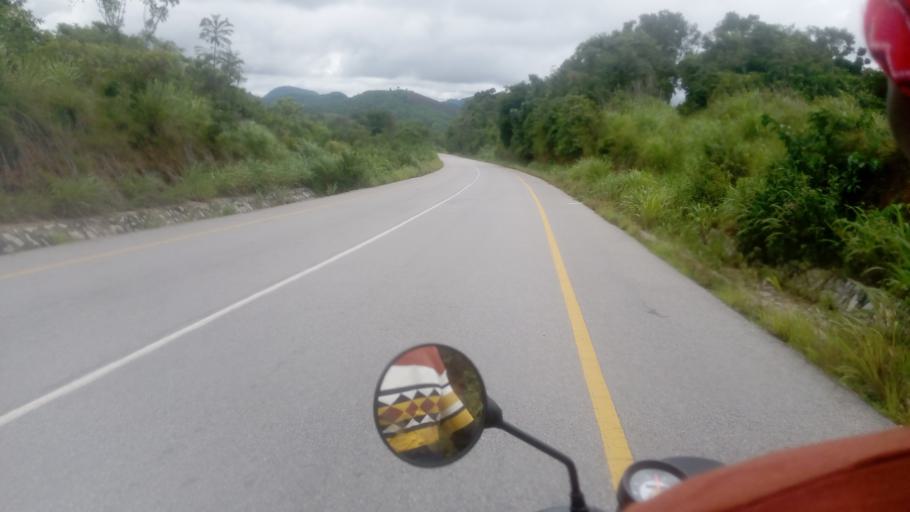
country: SL
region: Northern Province
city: Masaka
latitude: 8.6453
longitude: -11.7539
